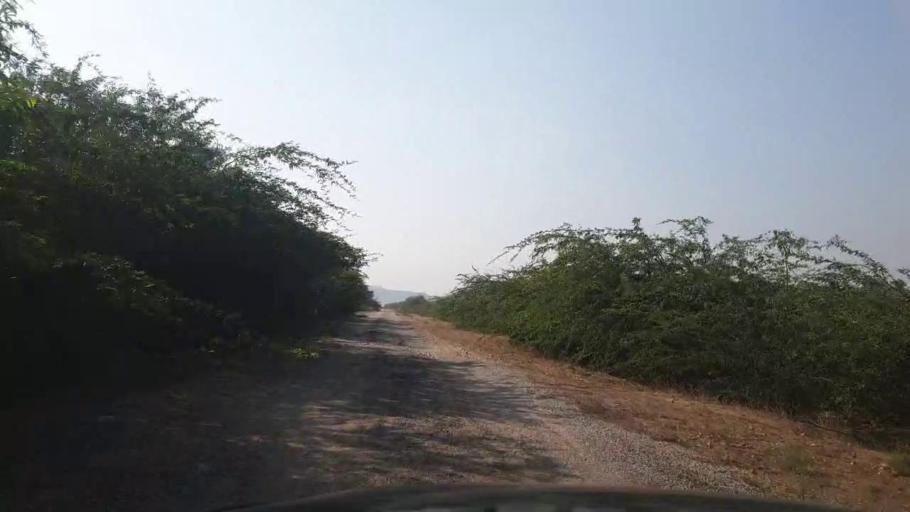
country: PK
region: Sindh
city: Gharo
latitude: 25.0567
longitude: 67.5600
